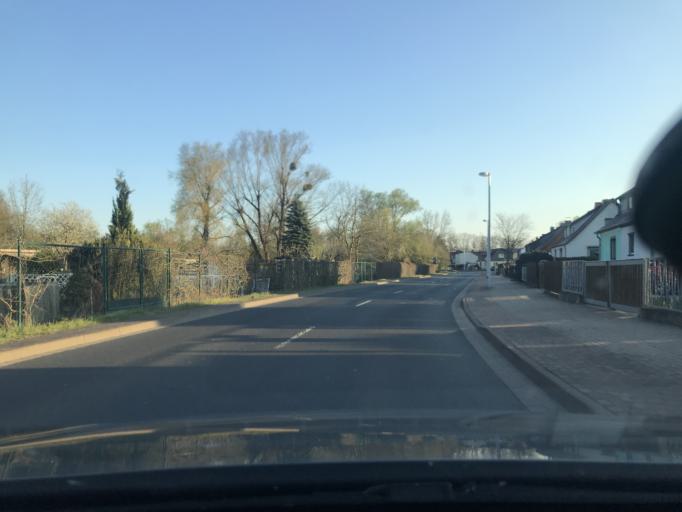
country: DE
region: Thuringia
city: Nordhausen
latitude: 51.4955
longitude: 10.7709
